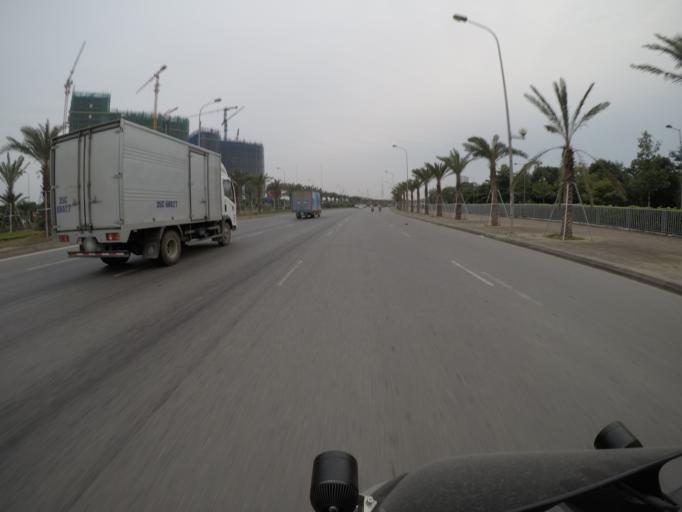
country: VN
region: Ha Noi
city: Thanh Xuan
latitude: 21.0027
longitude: 105.7857
